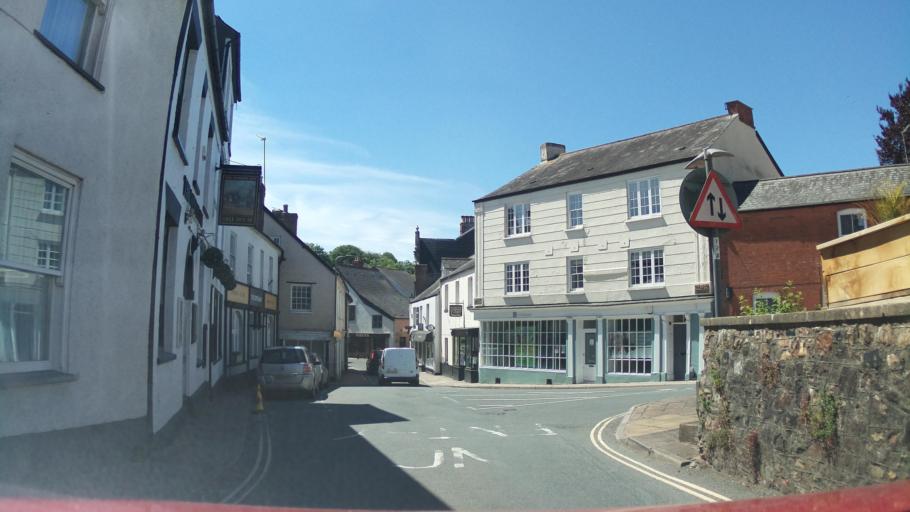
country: GB
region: England
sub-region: Devon
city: Ottery St Mary
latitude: 50.7519
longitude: -3.2787
